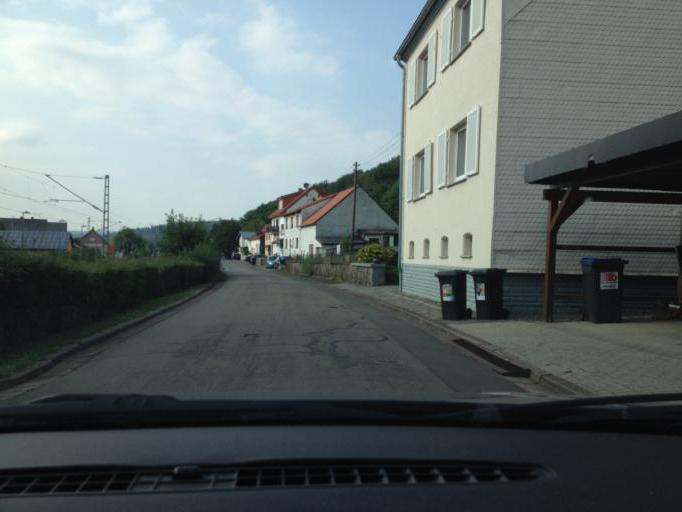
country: DE
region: Saarland
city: Nohfelden
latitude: 49.5571
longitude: 7.1306
